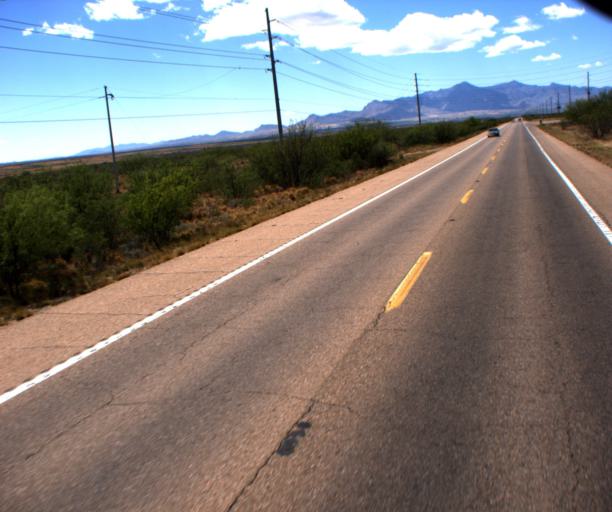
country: US
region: Arizona
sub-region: Cochise County
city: Naco
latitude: 31.3751
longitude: -110.0008
